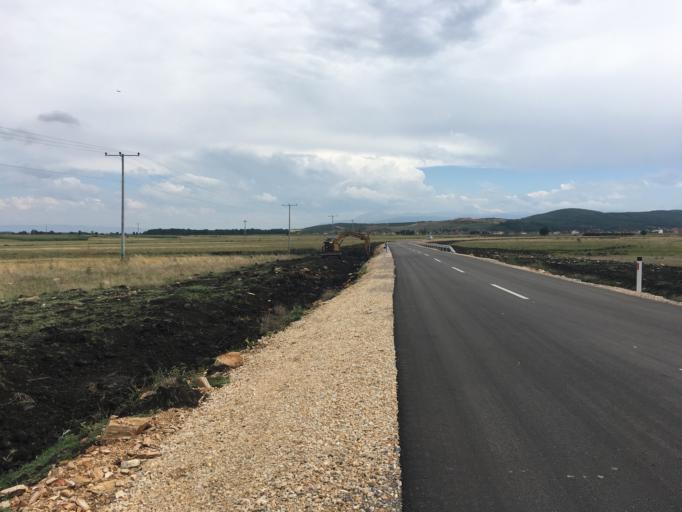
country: XK
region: Pristina
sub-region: Komuna e Gracanices
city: Glanica
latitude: 42.5485
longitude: 21.0205
